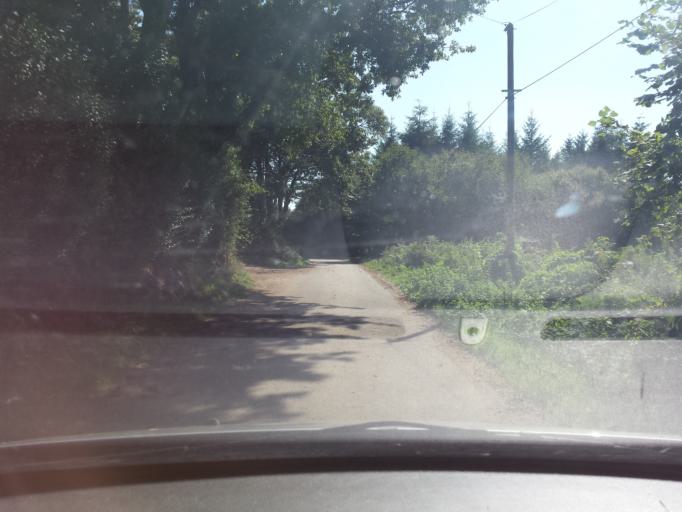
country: FR
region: Brittany
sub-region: Departement des Cotes-d'Armor
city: Plounevez-Quintin
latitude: 48.3315
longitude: -3.2666
